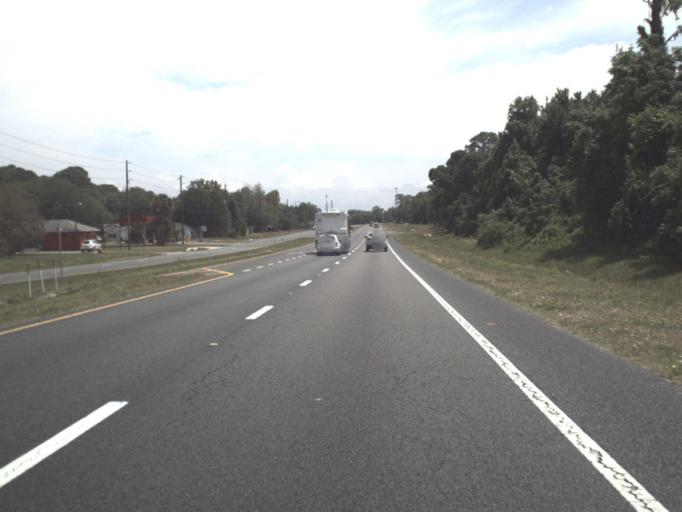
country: US
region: Florida
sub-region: Sumter County
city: Wildwood
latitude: 28.8297
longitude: -81.9964
